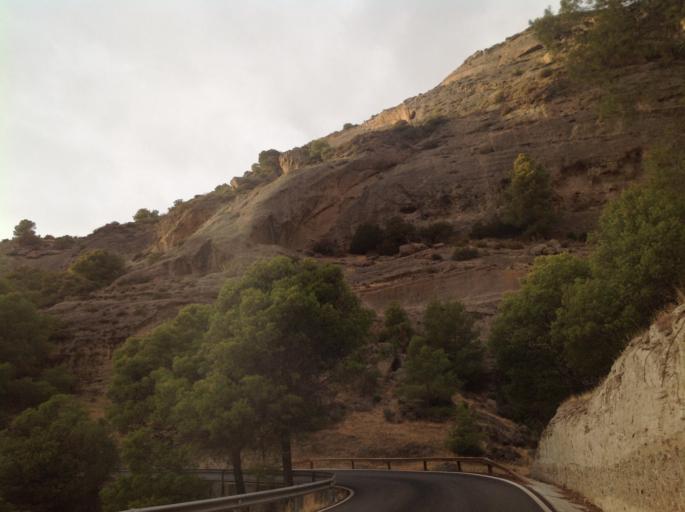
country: ES
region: Andalusia
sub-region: Provincia de Malaga
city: Ardales
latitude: 36.9134
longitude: -4.7902
